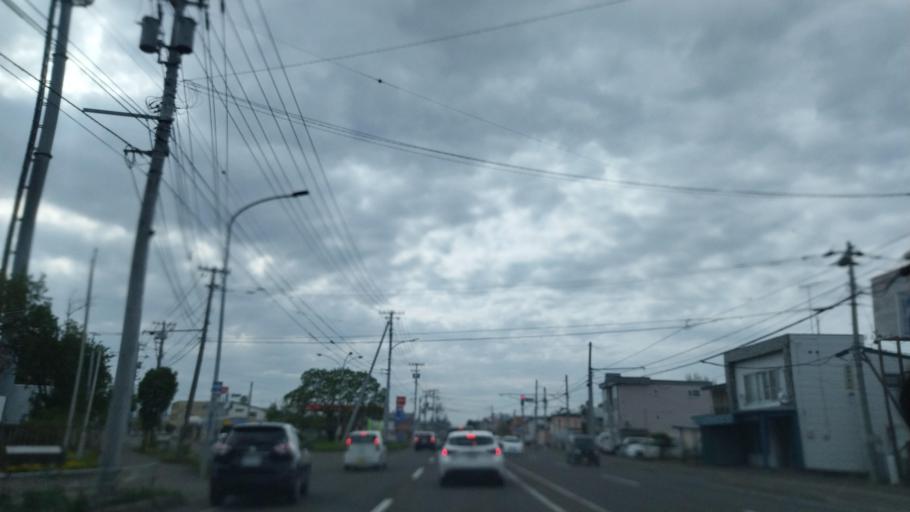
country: JP
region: Hokkaido
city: Obihiro
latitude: 42.9273
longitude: 143.2206
